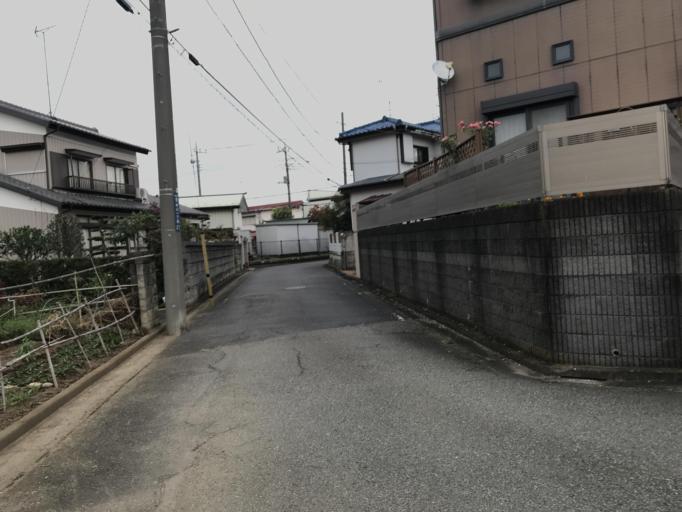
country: JP
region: Saitama
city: Hasuda
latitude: 35.9912
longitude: 139.6566
